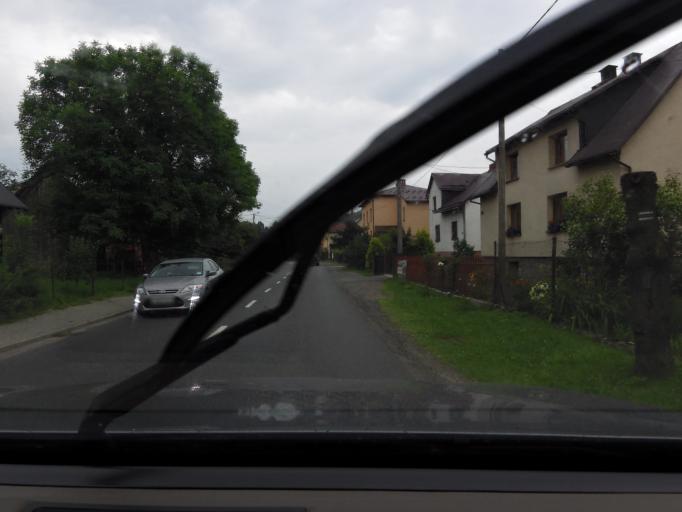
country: PL
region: Silesian Voivodeship
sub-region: Powiat zywiecki
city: Milowka
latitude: 49.5516
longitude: 19.0928
